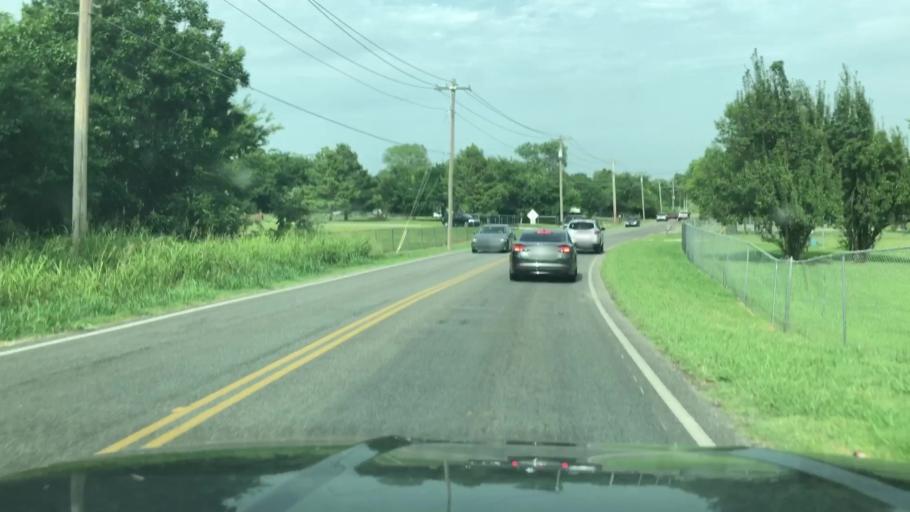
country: US
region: Oklahoma
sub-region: Tulsa County
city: Oakhurst
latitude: 36.0900
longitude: -96.0691
